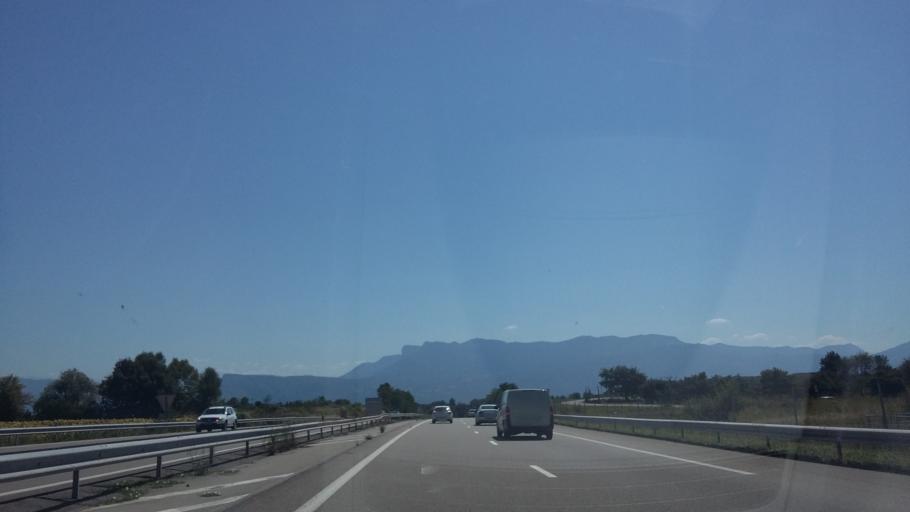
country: FR
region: Rhone-Alpes
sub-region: Departement de l'Isere
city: Apprieu
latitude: 45.3797
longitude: 5.4800
